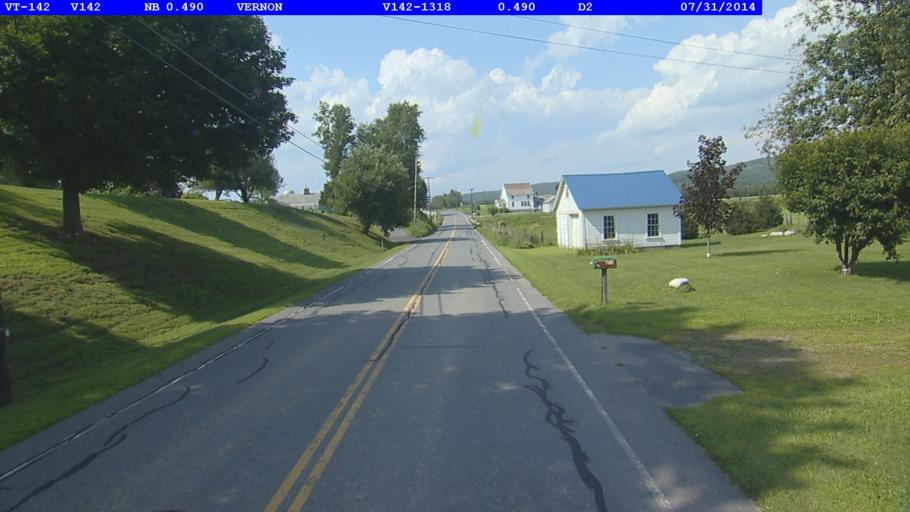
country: US
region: Massachusetts
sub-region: Franklin County
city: Northfield
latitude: 42.7332
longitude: -72.4689
